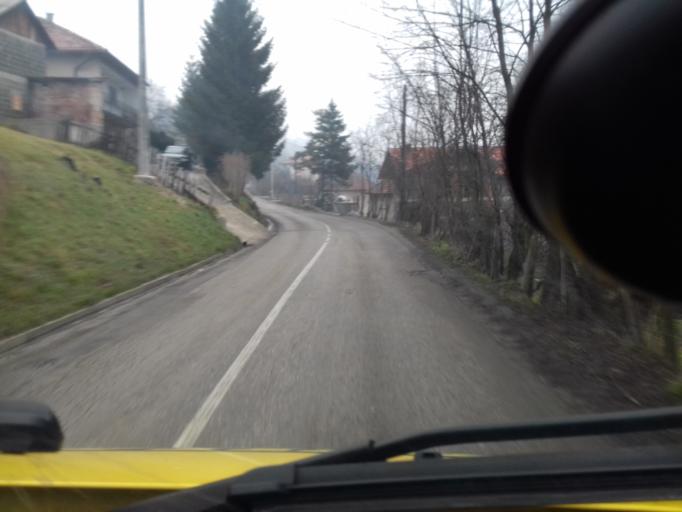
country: BA
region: Federation of Bosnia and Herzegovina
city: Lokvine
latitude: 44.1999
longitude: 17.8688
